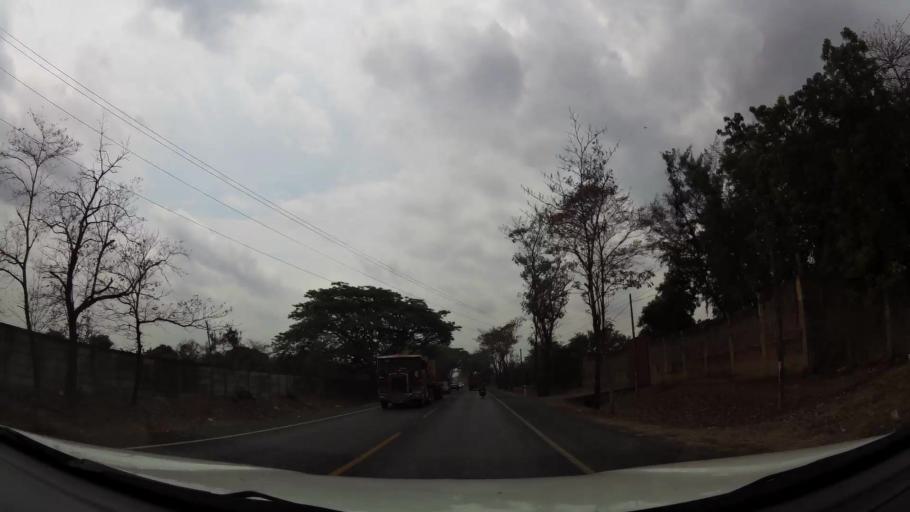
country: NI
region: Leon
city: Leon
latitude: 12.4736
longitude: -86.8637
